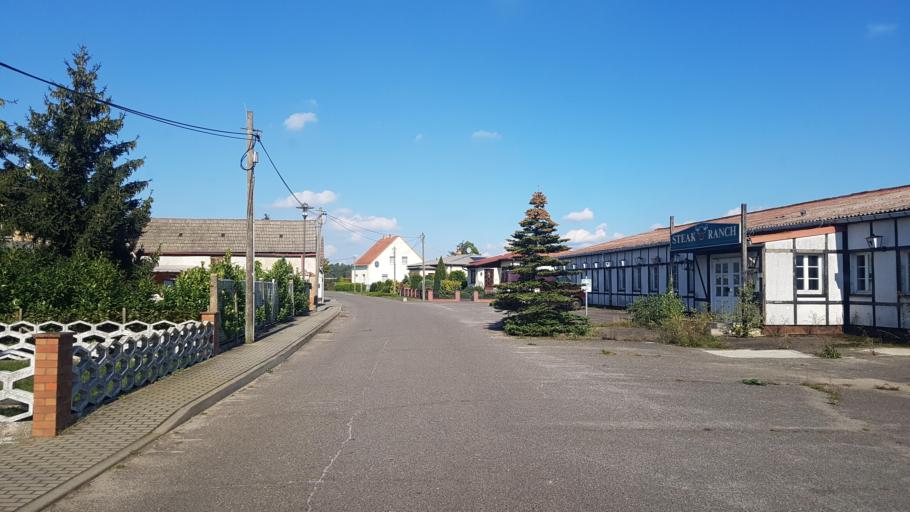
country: DE
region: Brandenburg
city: Ihlow
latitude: 51.8490
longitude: 13.2678
